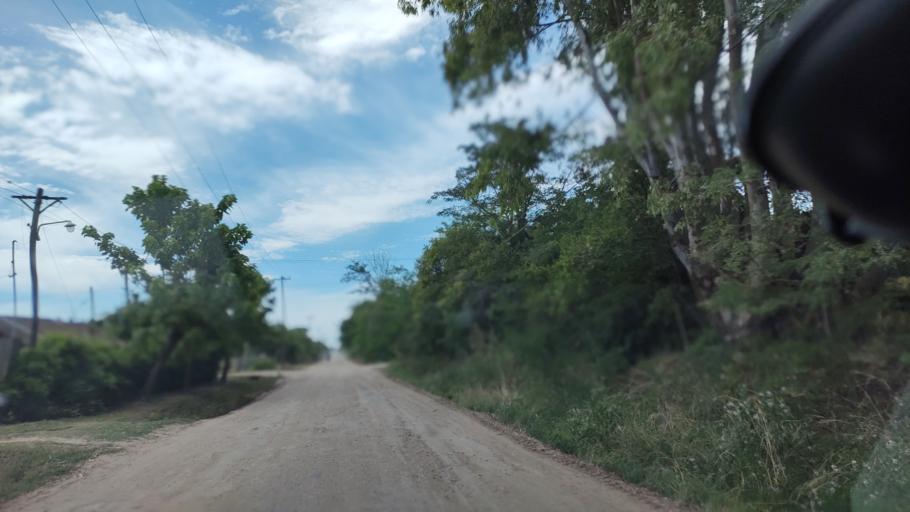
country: AR
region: Buenos Aires
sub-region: Partido de Lobos
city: Lobos
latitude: -35.1703
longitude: -59.1087
